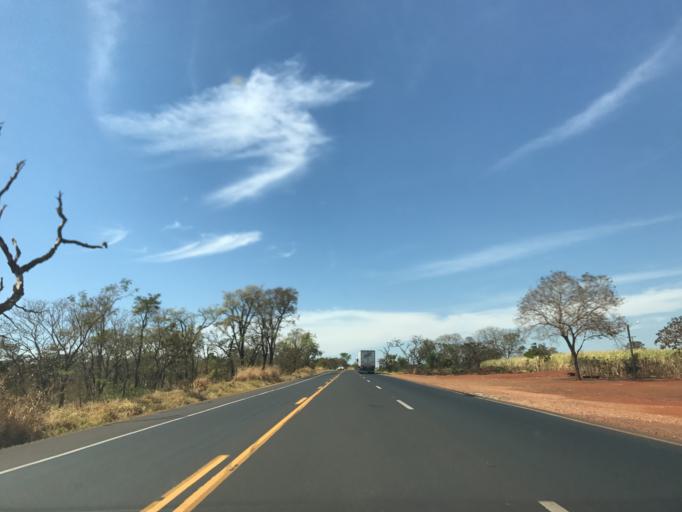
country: BR
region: Minas Gerais
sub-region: Prata
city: Prata
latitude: -19.0947
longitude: -48.9859
